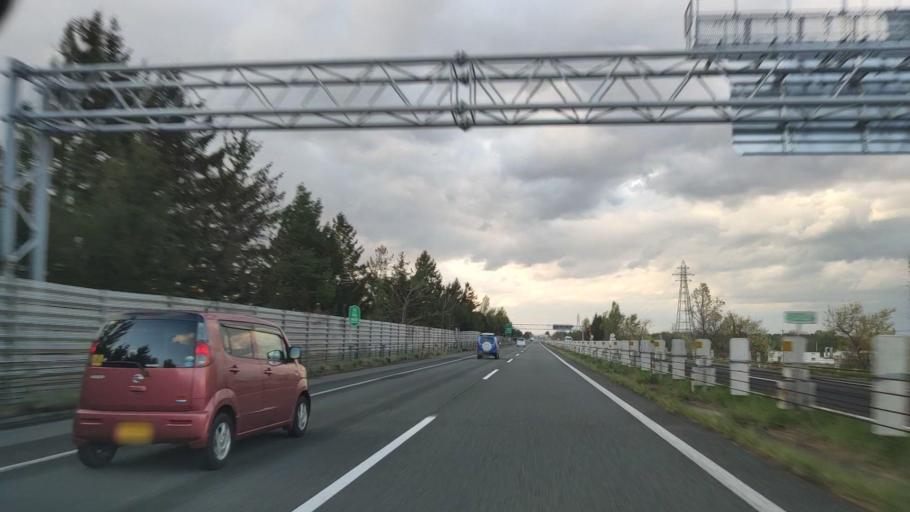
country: JP
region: Iwate
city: Kitakami
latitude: 39.2815
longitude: 141.0801
